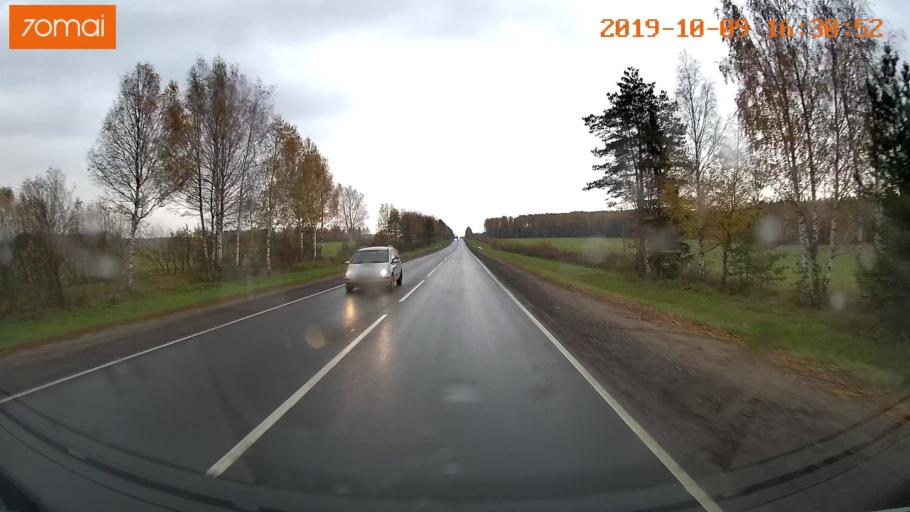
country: RU
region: Kostroma
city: Oktyabr'skiy
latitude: 57.6136
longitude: 40.9451
